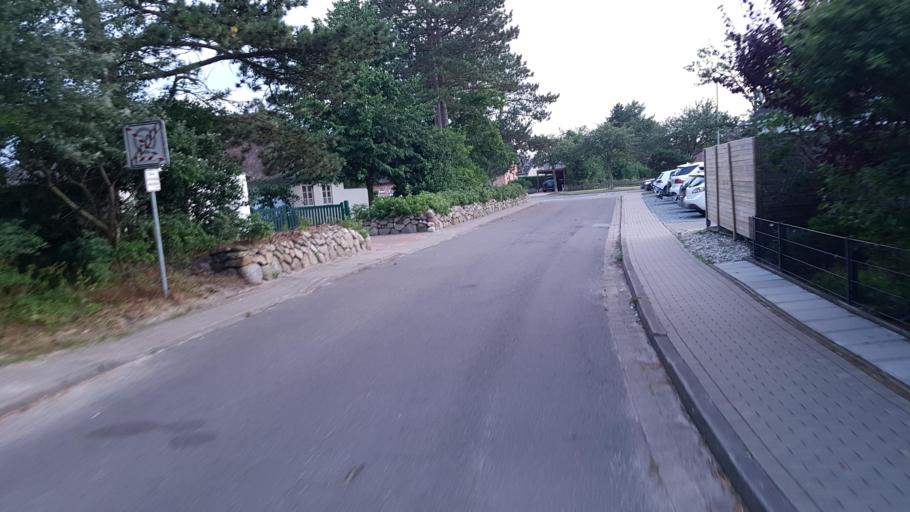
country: DE
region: Schleswig-Holstein
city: Sankt Peter-Ording
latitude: 54.2975
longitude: 8.6461
